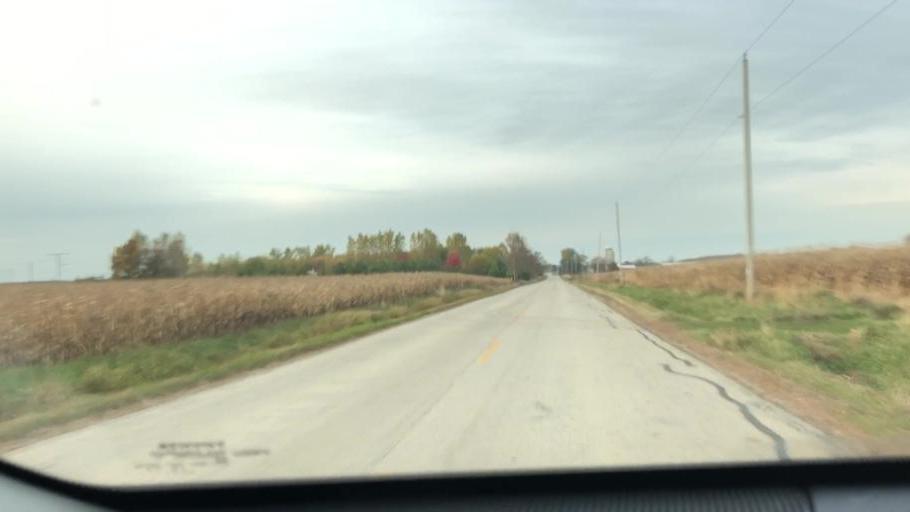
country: US
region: Wisconsin
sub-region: Outagamie County
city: Seymour
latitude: 44.4524
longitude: -88.3502
